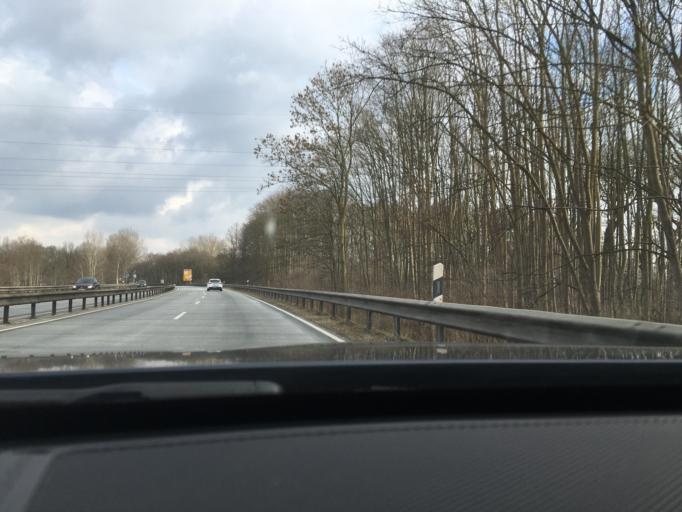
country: DE
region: Lower Saxony
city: Stuhr
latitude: 53.0467
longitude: 8.7063
